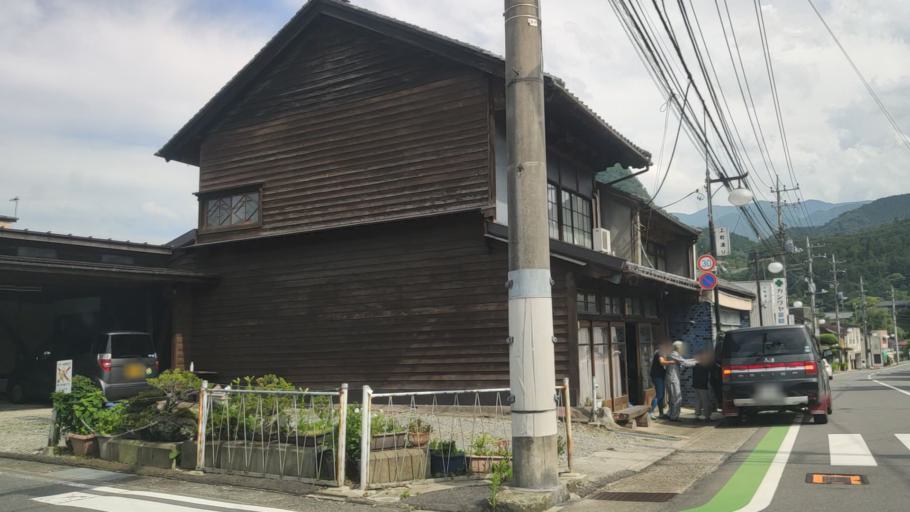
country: JP
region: Gunma
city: Tomioka
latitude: 36.2101
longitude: 138.7827
